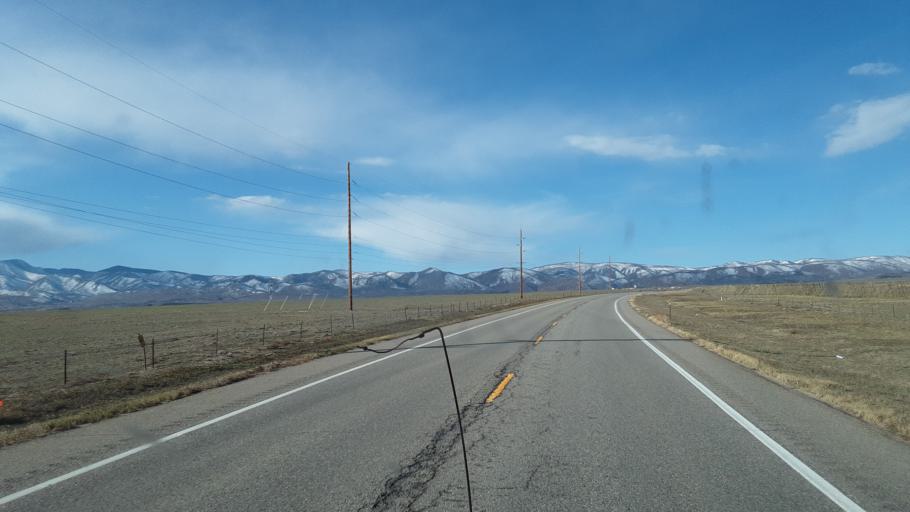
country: US
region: Colorado
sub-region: Huerfano County
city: Walsenburg
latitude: 37.5447
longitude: -105.0034
